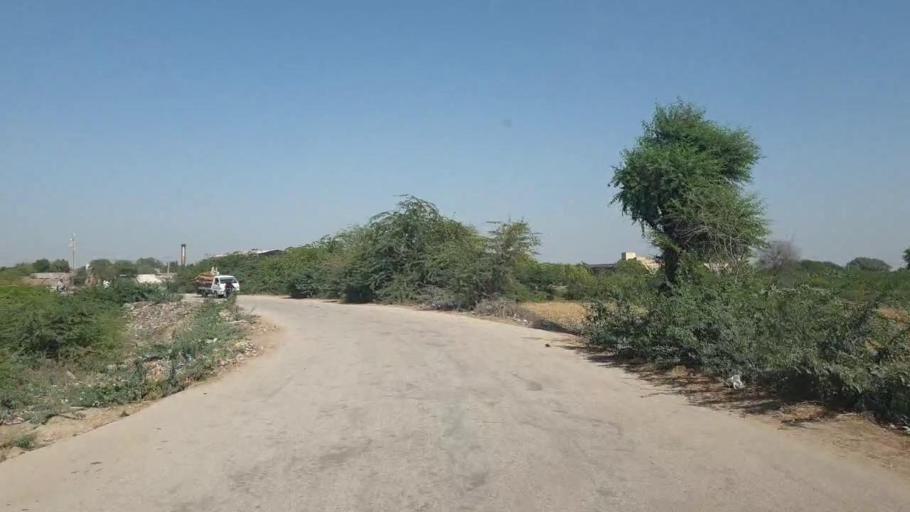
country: PK
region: Sindh
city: Talhar
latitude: 24.8779
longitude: 68.8175
